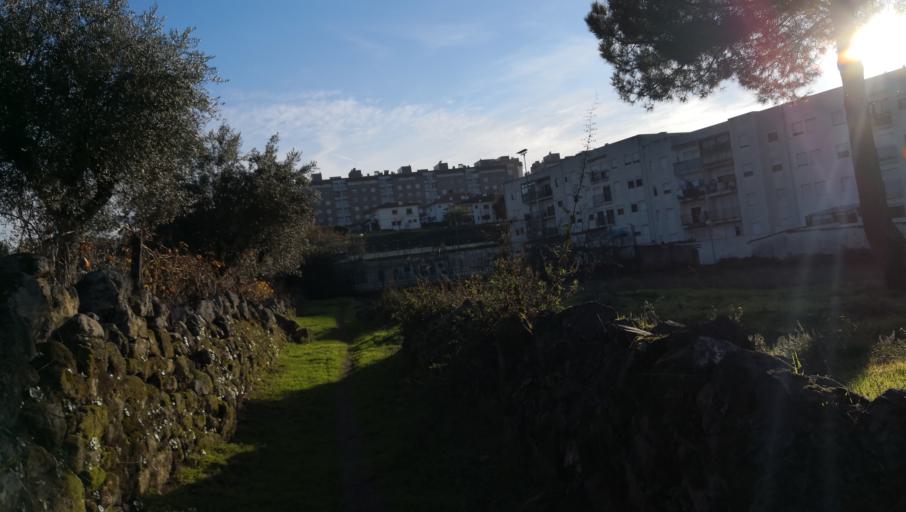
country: PT
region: Vila Real
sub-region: Vila Real
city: Vila Real
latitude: 41.3089
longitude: -7.7210
